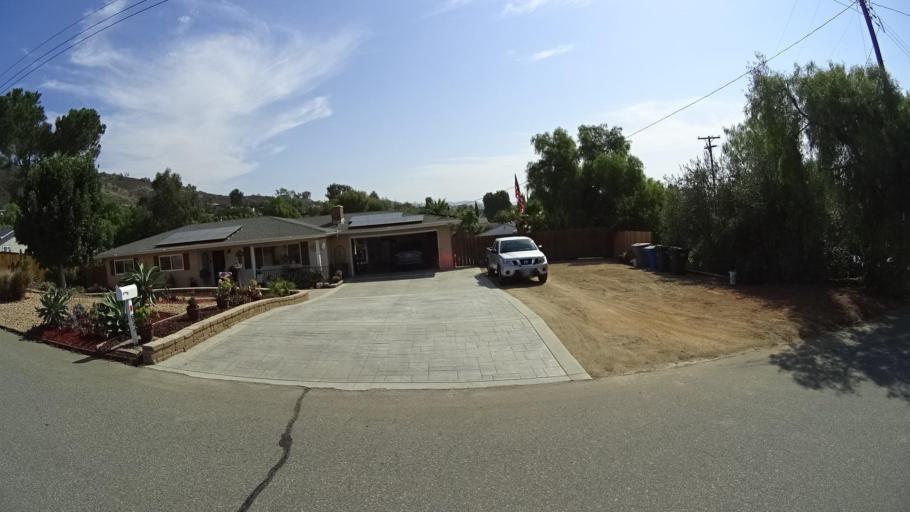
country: US
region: California
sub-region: San Diego County
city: San Marcos
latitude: 33.1572
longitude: -117.1381
